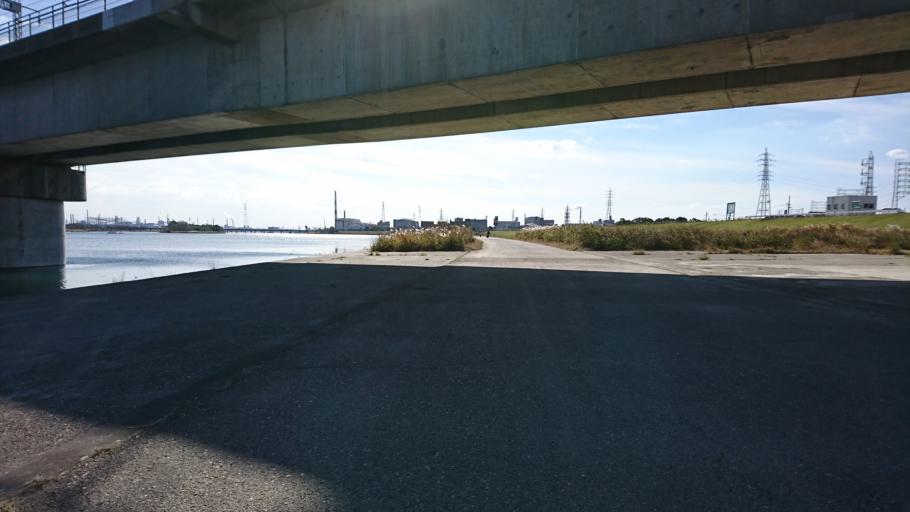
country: JP
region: Hyogo
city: Kakogawacho-honmachi
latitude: 34.7618
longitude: 134.8062
